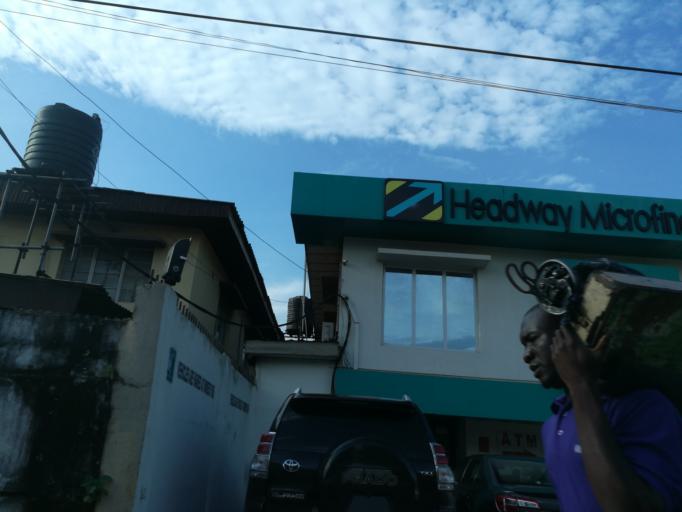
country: NG
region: Lagos
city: Ikeja
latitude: 6.5957
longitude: 3.3462
